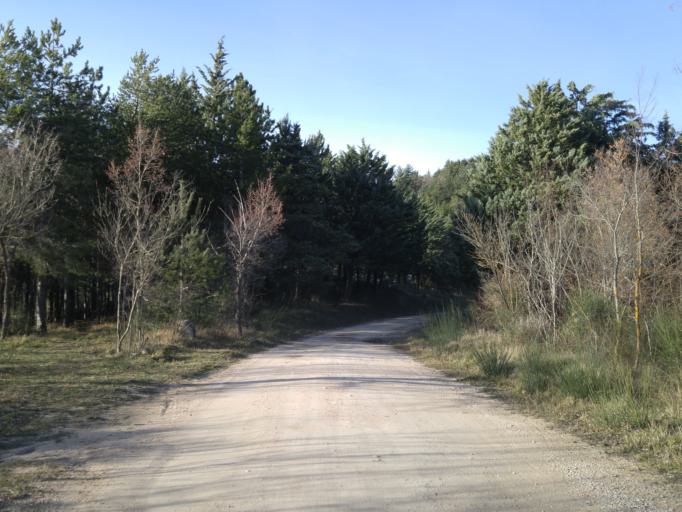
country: IT
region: The Marches
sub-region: Provincia di Pesaro e Urbino
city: Canavaccio
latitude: 43.6755
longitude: 12.6815
